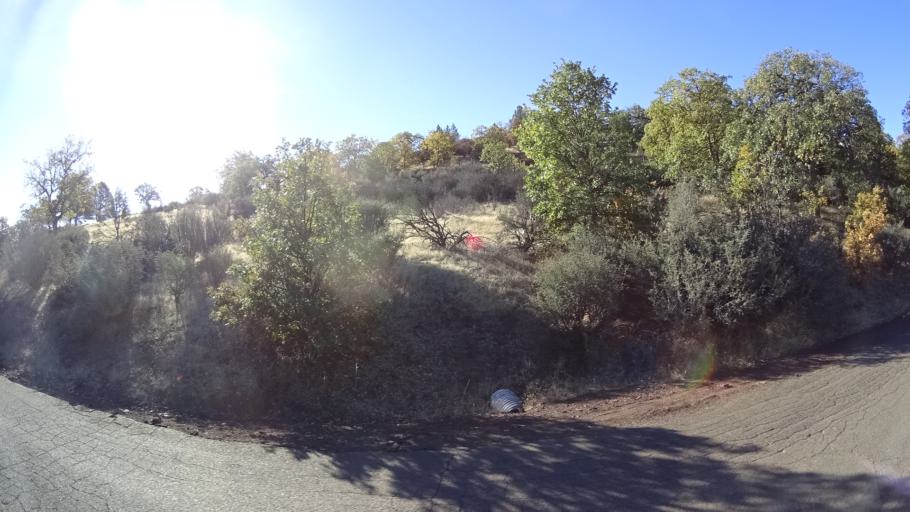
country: US
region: California
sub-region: Siskiyou County
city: Montague
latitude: 41.9616
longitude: -122.4412
